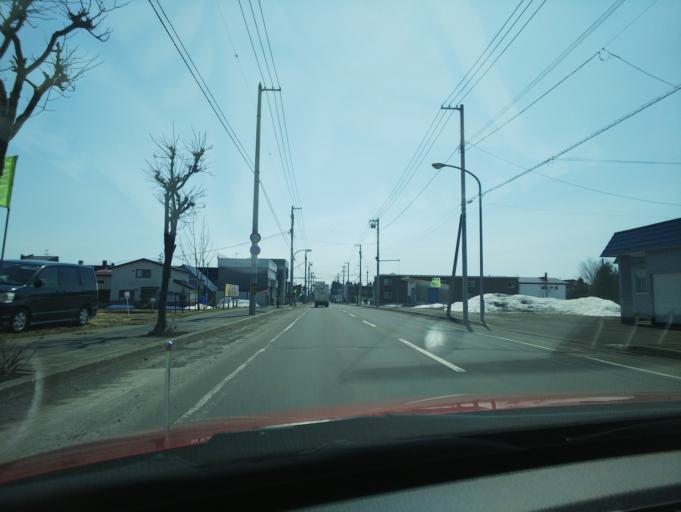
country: JP
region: Hokkaido
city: Nayoro
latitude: 44.3429
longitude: 142.4643
